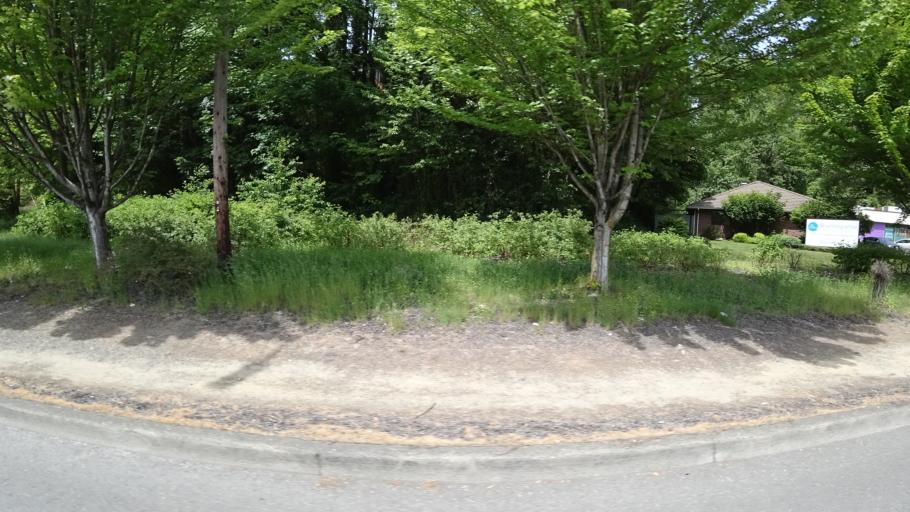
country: US
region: Oregon
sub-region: Clackamas County
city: Lake Oswego
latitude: 45.4711
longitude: -122.6878
